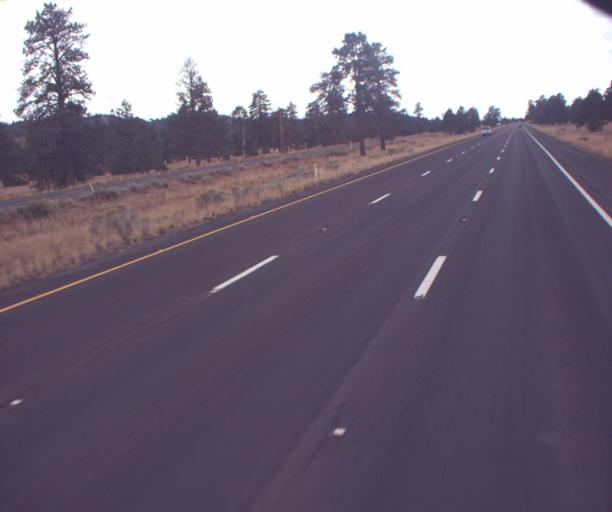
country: US
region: Arizona
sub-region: Coconino County
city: Flagstaff
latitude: 35.3950
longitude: -111.5778
